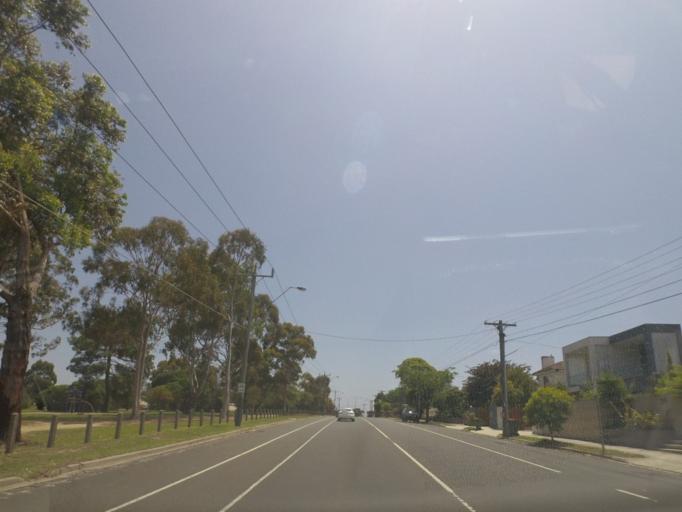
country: AU
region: Victoria
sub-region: Bayside
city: Hampton East
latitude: -37.9275
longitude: 145.0264
